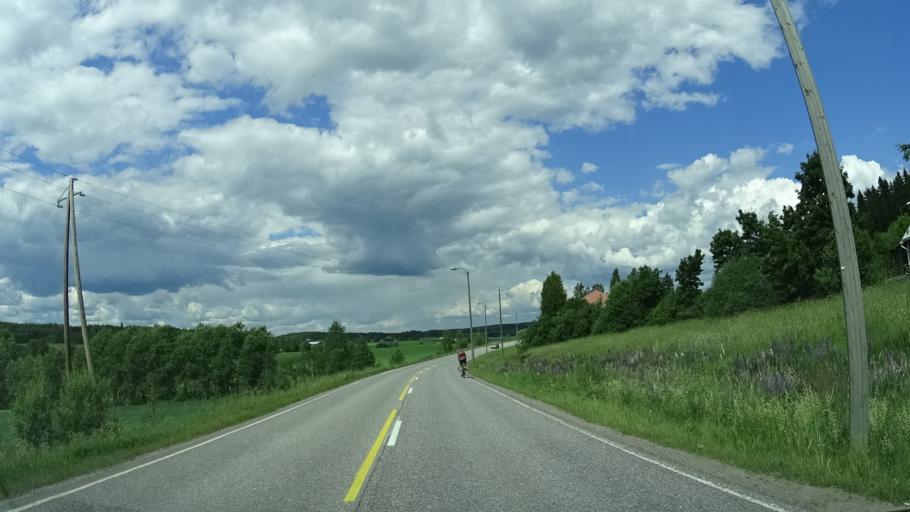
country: FI
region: Uusimaa
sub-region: Helsinki
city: Nurmijaervi
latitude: 60.3881
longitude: 24.6453
